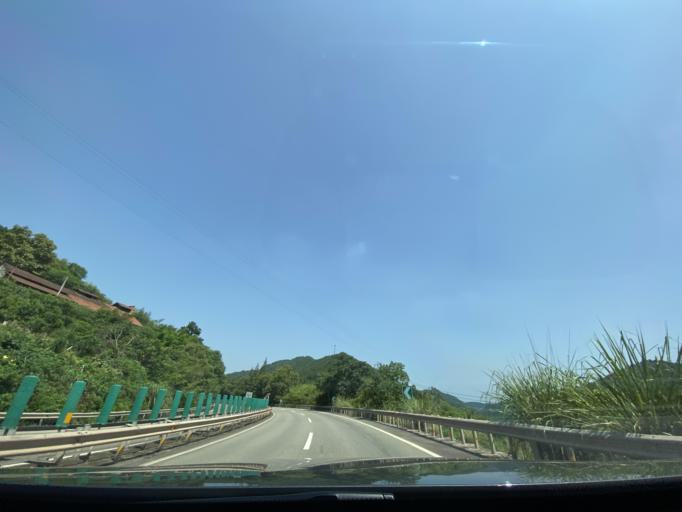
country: CN
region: Sichuan
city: Longquan
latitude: 30.5532
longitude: 104.3538
